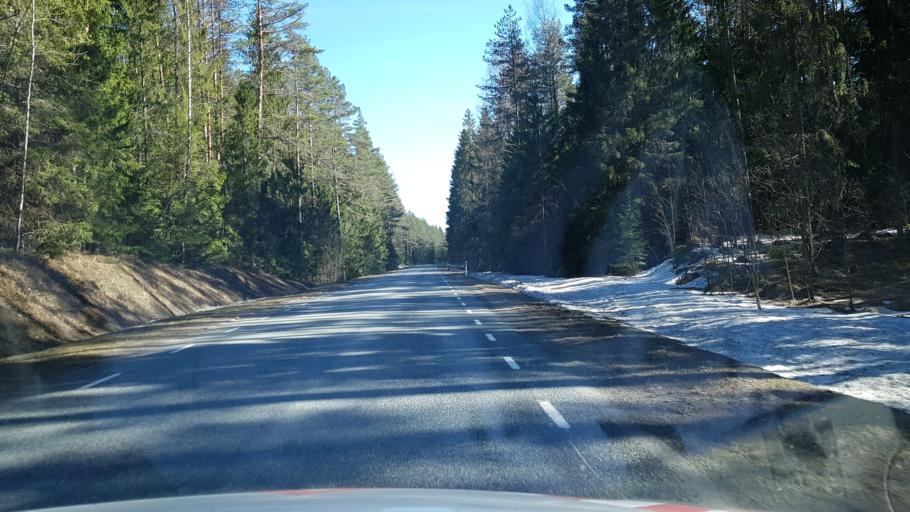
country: EE
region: Laeaene-Virumaa
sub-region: Vinni vald
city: Vinni
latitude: 59.2605
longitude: 26.6821
